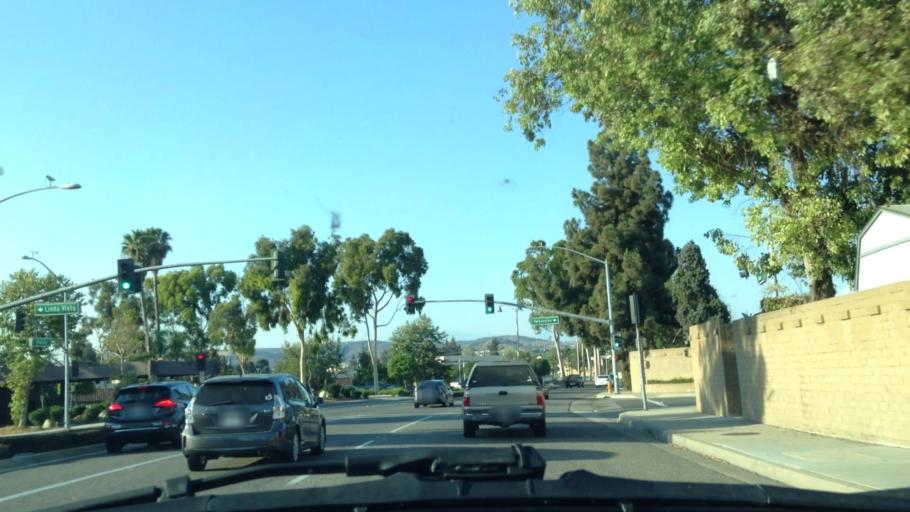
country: US
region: California
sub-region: Orange County
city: Placentia
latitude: 33.8844
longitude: -117.8437
